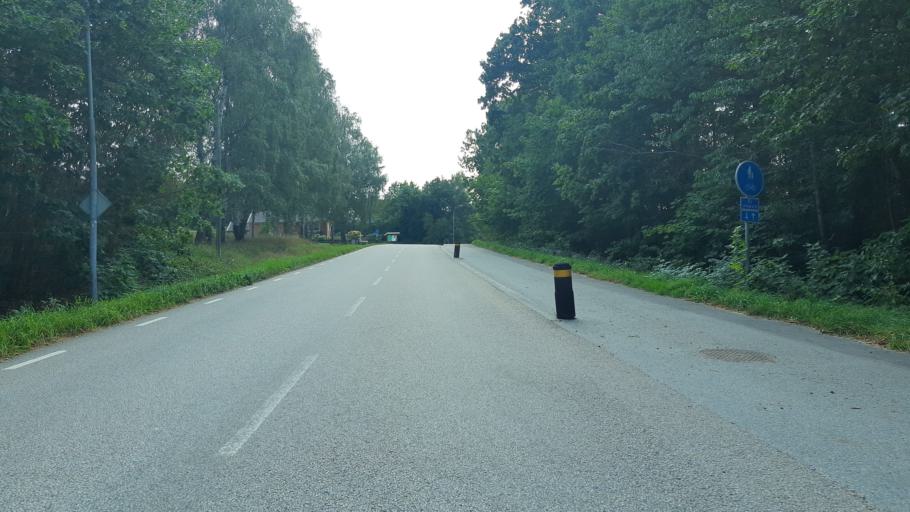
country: SE
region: Blekinge
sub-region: Karlskrona Kommun
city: Nattraby
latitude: 56.2217
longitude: 15.4135
